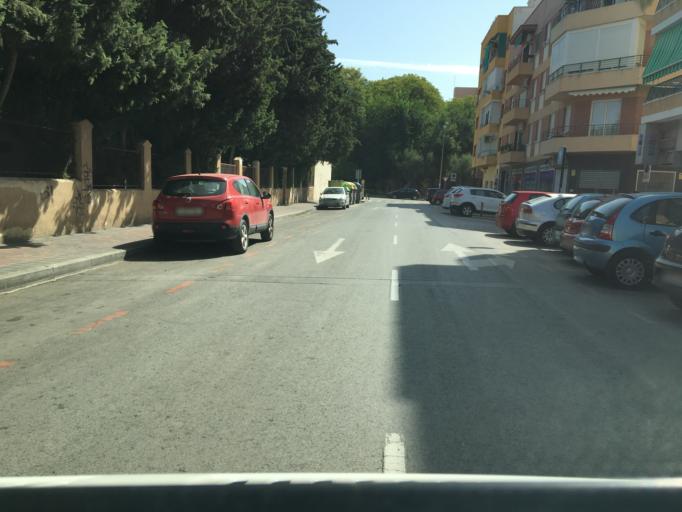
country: ES
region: Murcia
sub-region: Murcia
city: Murcia
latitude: 37.9967
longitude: -1.1284
